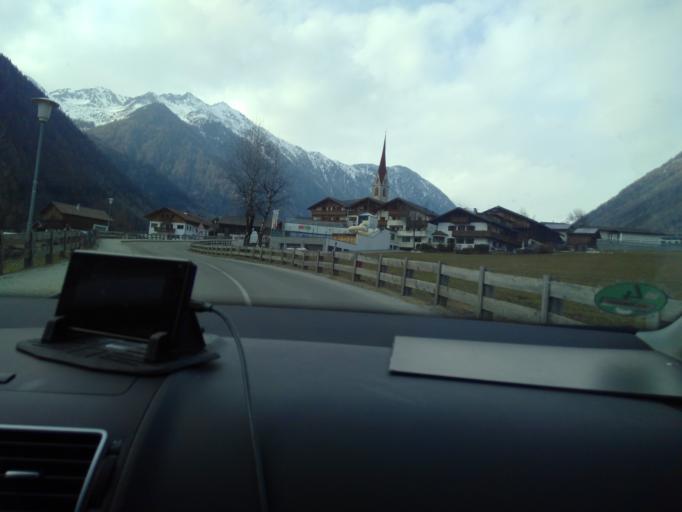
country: IT
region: Trentino-Alto Adige
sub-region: Bolzano
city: Fortezza
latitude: 46.8375
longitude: 11.6283
